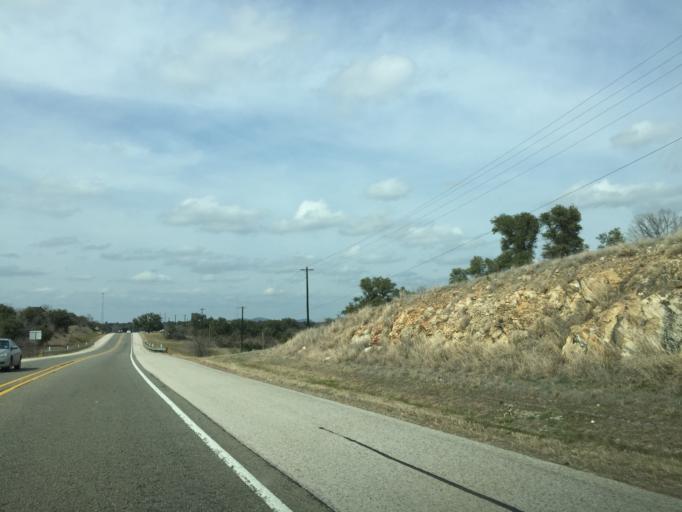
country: US
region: Texas
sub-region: Burnet County
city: Granite Shoals
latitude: 30.5213
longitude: -98.4130
